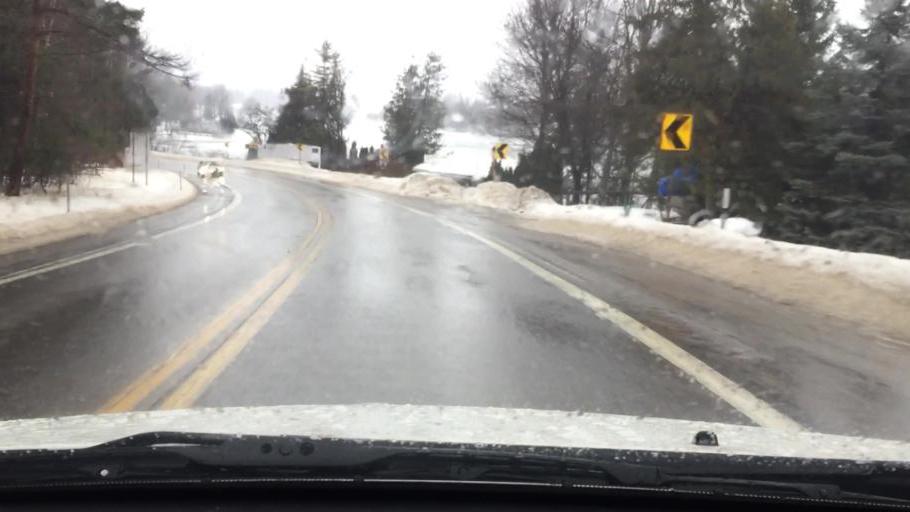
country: US
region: Michigan
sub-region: Charlevoix County
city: Charlevoix
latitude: 45.2478
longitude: -85.1807
